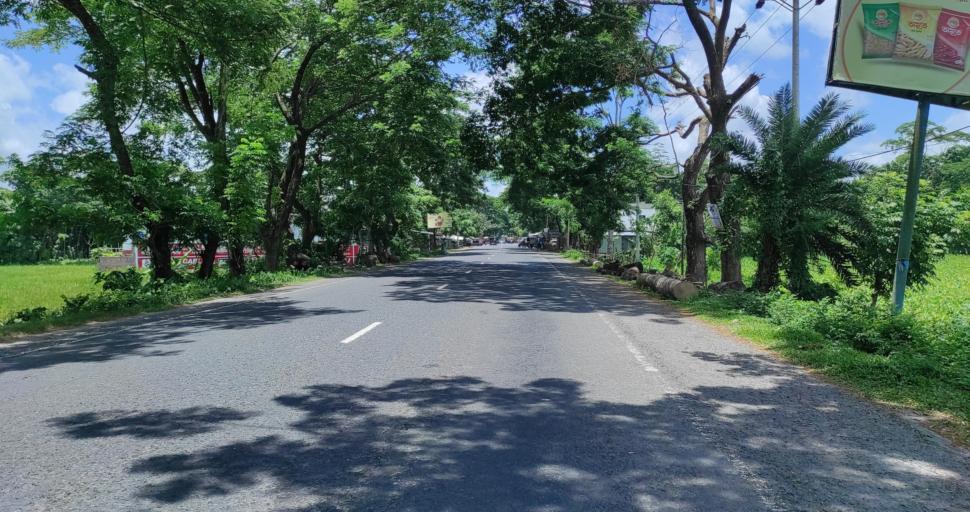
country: BD
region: Barisal
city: Barisal
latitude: 22.8188
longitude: 90.2714
